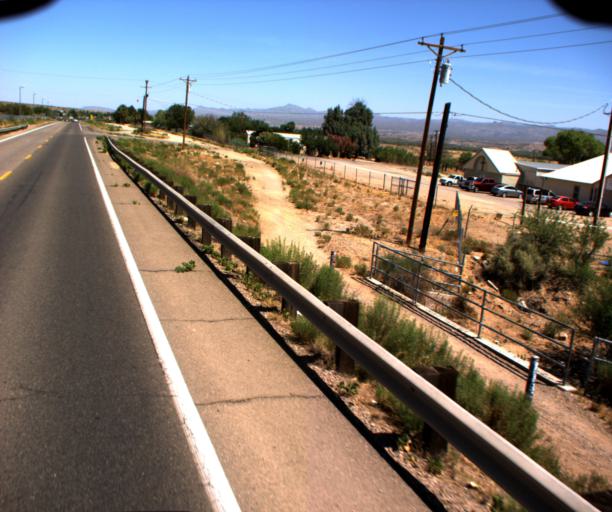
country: US
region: Arizona
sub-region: Graham County
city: Bylas
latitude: 33.1316
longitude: -110.1197
